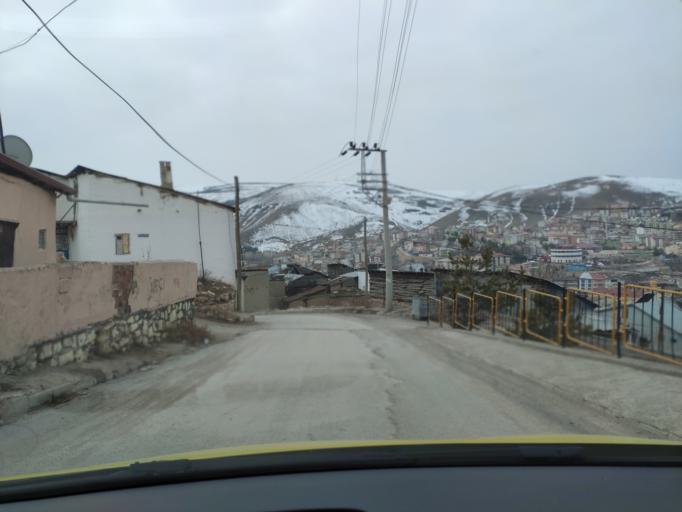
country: TR
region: Bayburt
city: Bayburt
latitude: 40.2567
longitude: 40.2300
